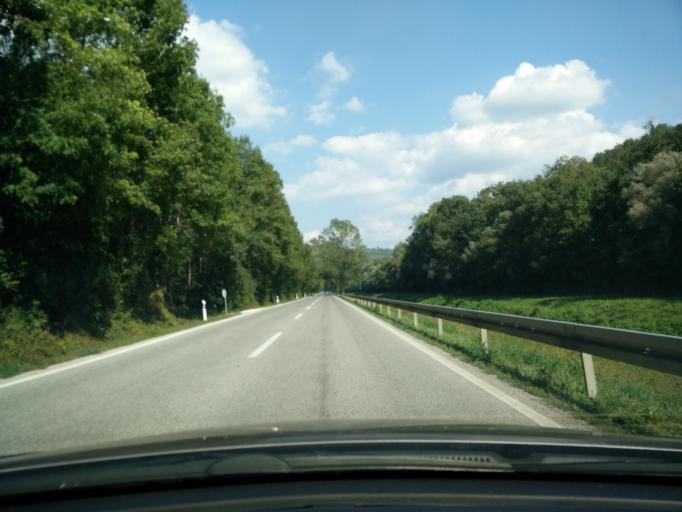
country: HR
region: Istarska
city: Karojba
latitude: 45.3675
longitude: 13.8763
